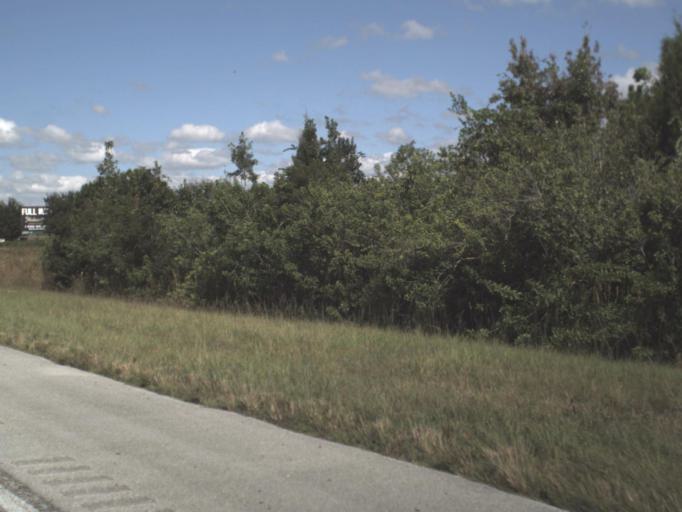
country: US
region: Florida
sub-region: Osceola County
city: Saint Cloud
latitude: 28.2169
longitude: -81.3124
